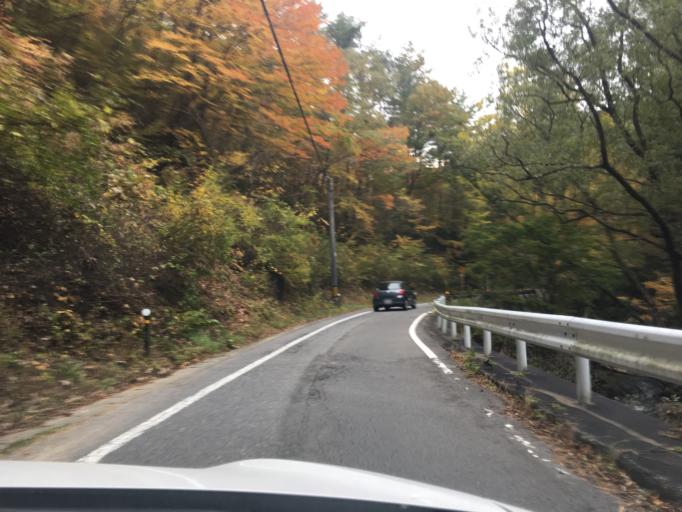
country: JP
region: Fukushima
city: Iwaki
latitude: 37.1618
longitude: 140.7347
